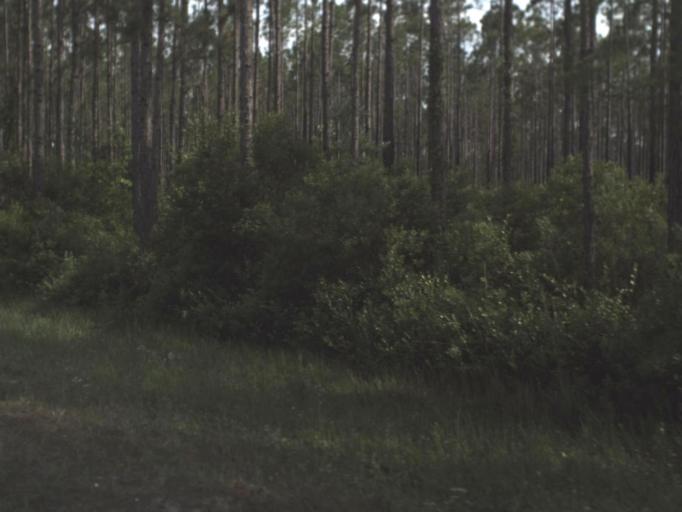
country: US
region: Florida
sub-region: Columbia County
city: Five Points
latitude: 30.5729
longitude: -82.4556
